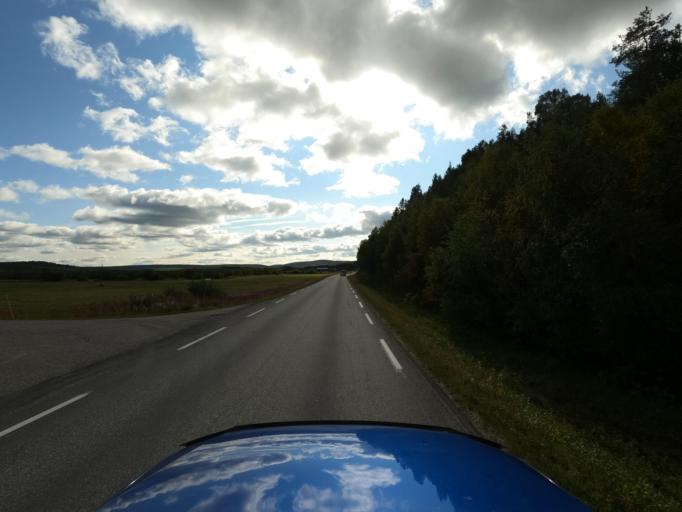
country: NO
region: Finnmark Fylke
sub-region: Karasjok
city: Karasjohka
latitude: 69.4106
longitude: 25.8052
